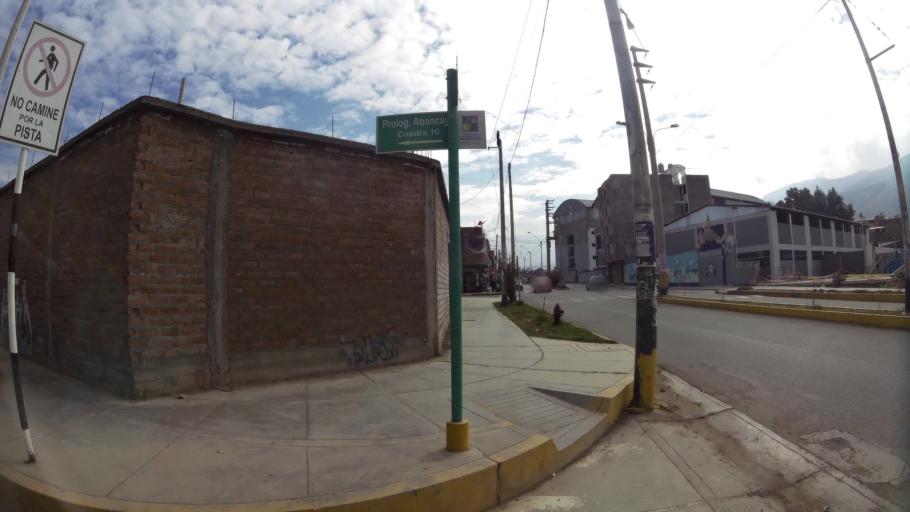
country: PE
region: Junin
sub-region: Provincia de Huancayo
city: Huancayo
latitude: -12.0589
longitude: -75.2010
